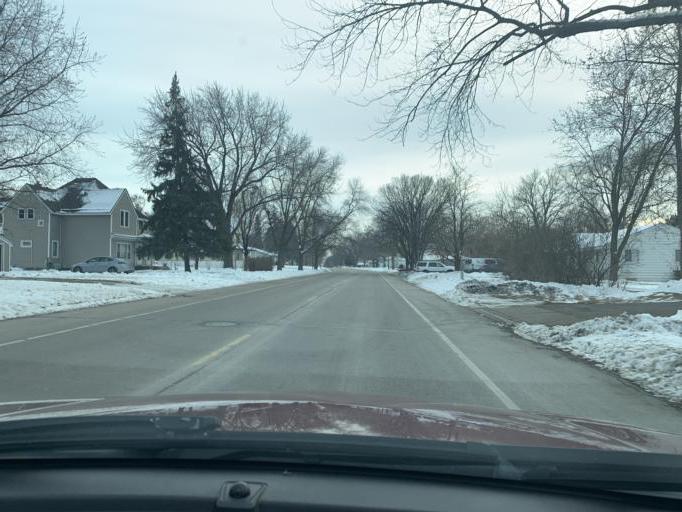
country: US
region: Minnesota
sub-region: Washington County
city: Saint Paul Park
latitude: 44.8415
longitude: -92.9914
